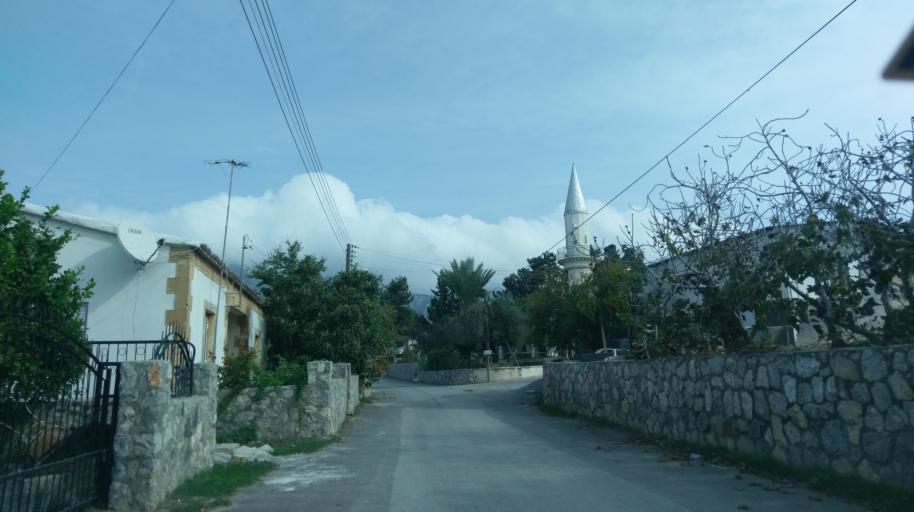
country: CY
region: Keryneia
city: Lapithos
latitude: 35.3002
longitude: 33.1066
